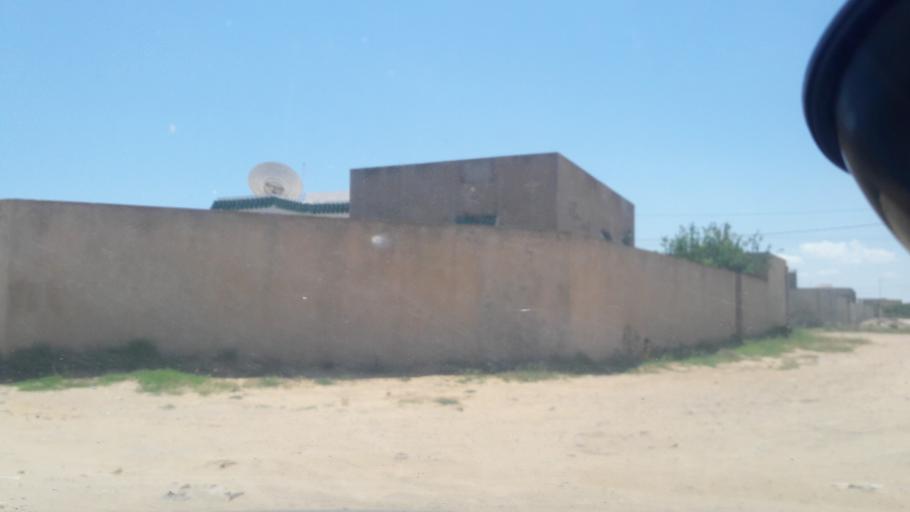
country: TN
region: Safaqis
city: Al Qarmadah
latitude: 34.8017
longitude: 10.7501
